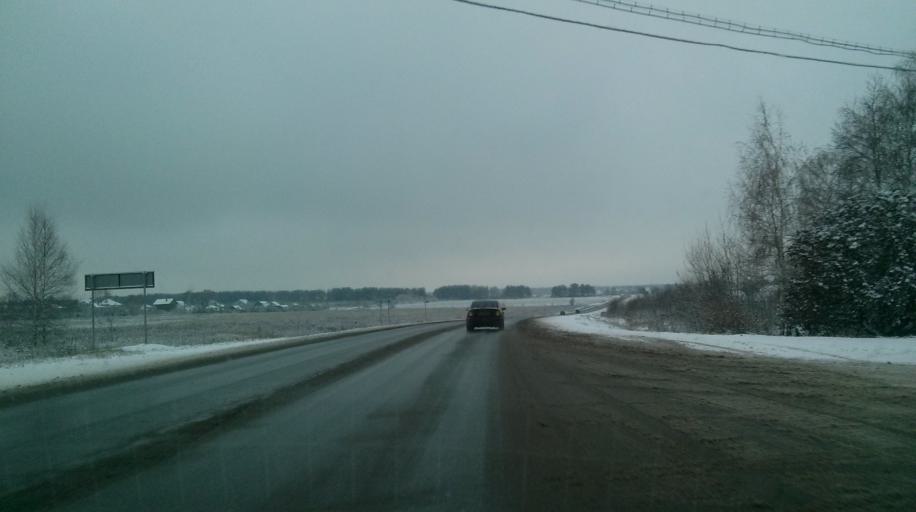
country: RU
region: Nizjnij Novgorod
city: Bogorodsk
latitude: 56.0871
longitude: 43.5286
